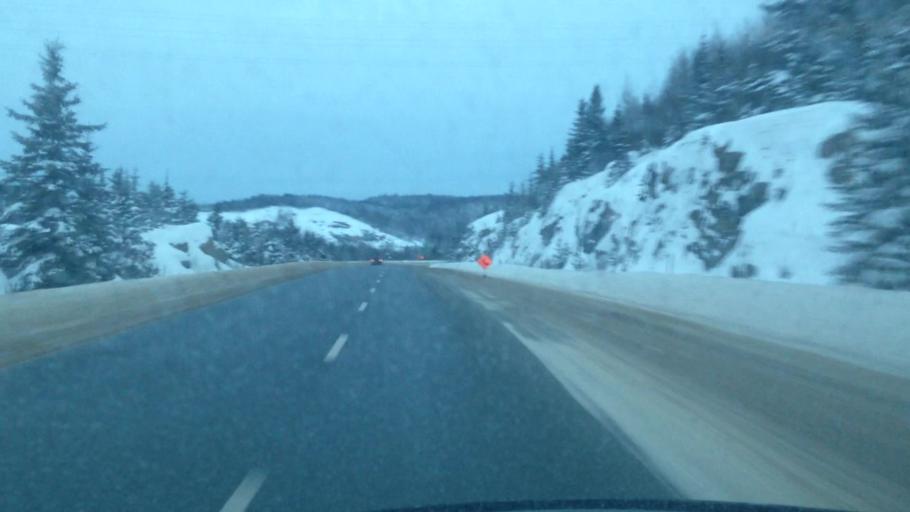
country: CA
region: Quebec
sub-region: Laurentides
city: Mont-Tremblant
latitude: 46.1170
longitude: -74.4647
